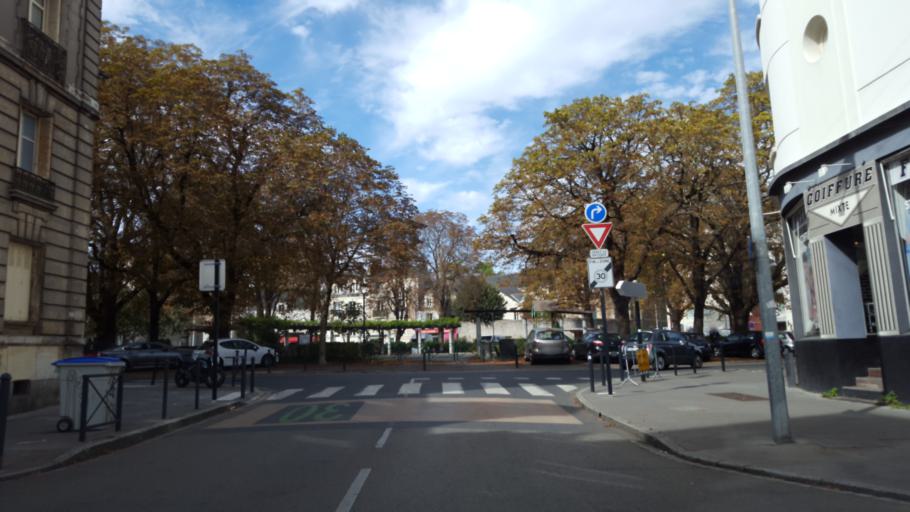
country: FR
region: Pays de la Loire
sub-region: Departement de la Loire-Atlantique
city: Nantes
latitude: 47.2140
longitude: -1.5740
